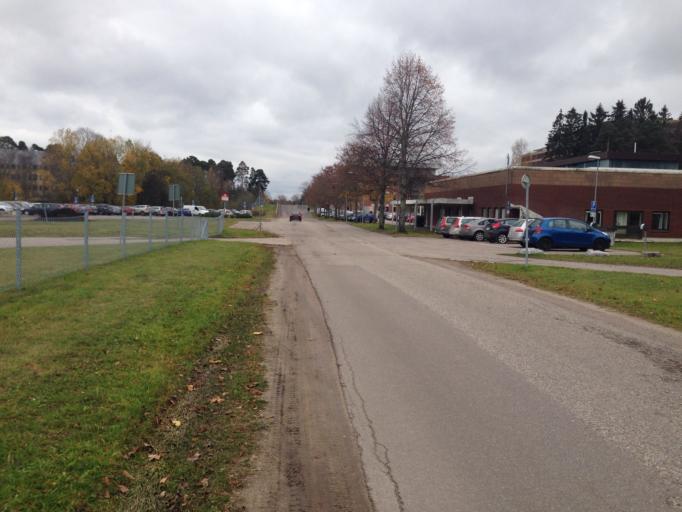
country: SE
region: Gaevleborg
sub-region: Gavle Kommun
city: Gavle
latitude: 60.6811
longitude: 17.1176
